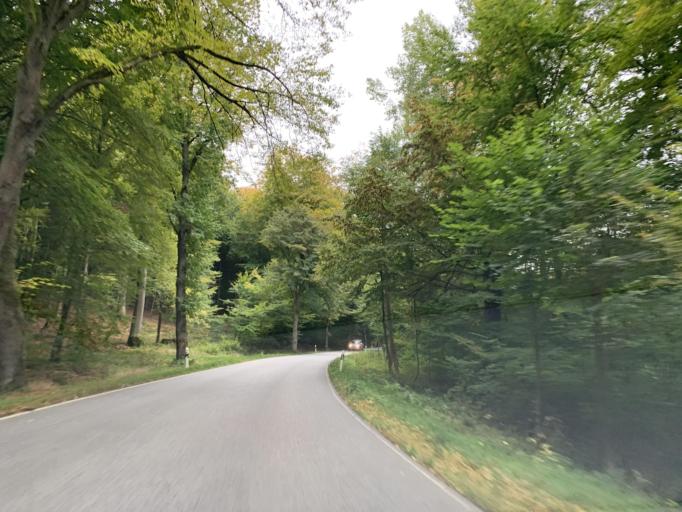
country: DE
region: Mecklenburg-Vorpommern
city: Burg Stargard
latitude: 53.4816
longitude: 13.2958
